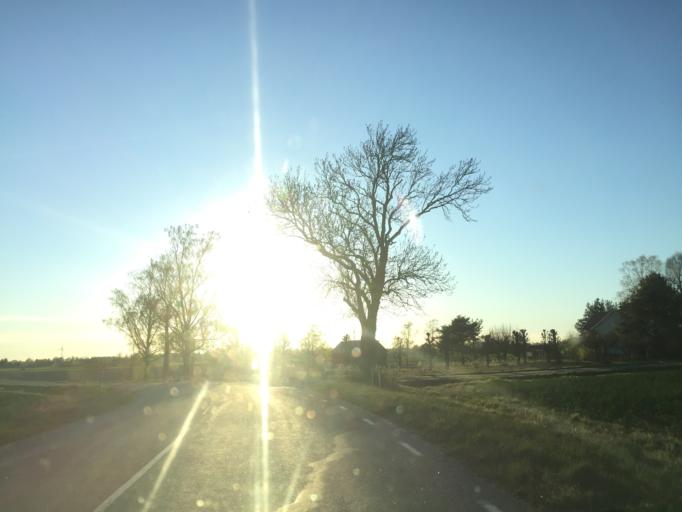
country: SE
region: OErebro
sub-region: Orebro Kommun
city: Odensbacken
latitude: 59.2050
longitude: 15.5204
